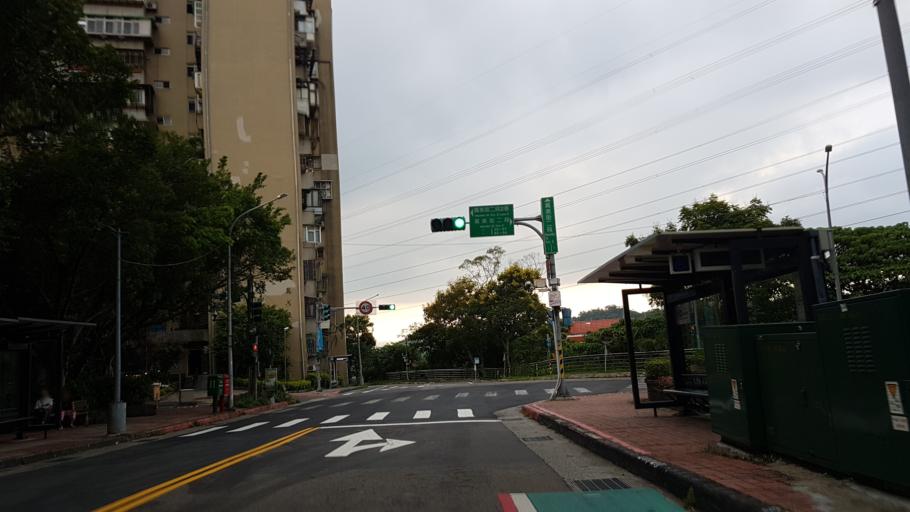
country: TW
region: Taipei
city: Taipei
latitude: 25.0034
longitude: 121.5633
